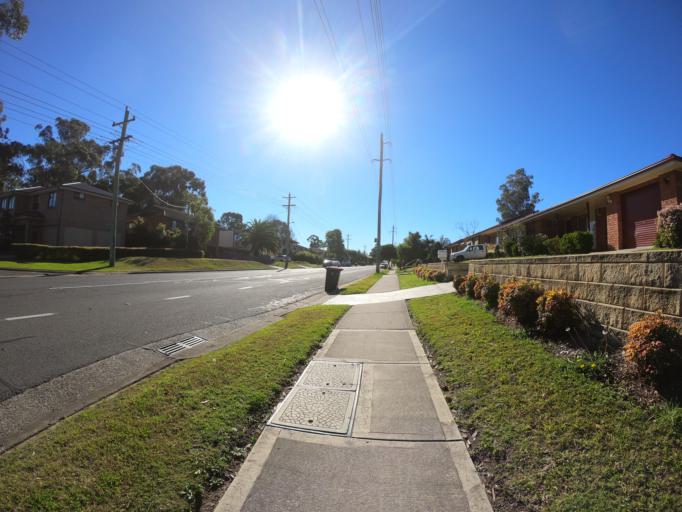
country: AU
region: New South Wales
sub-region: Hawkesbury
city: South Windsor
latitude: -33.6300
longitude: 150.7970
